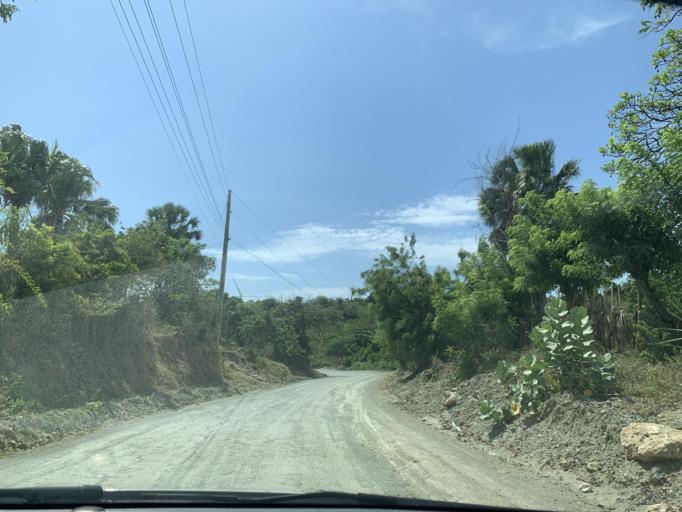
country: DO
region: Puerto Plata
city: Imbert
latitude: 19.8675
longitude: -70.8188
